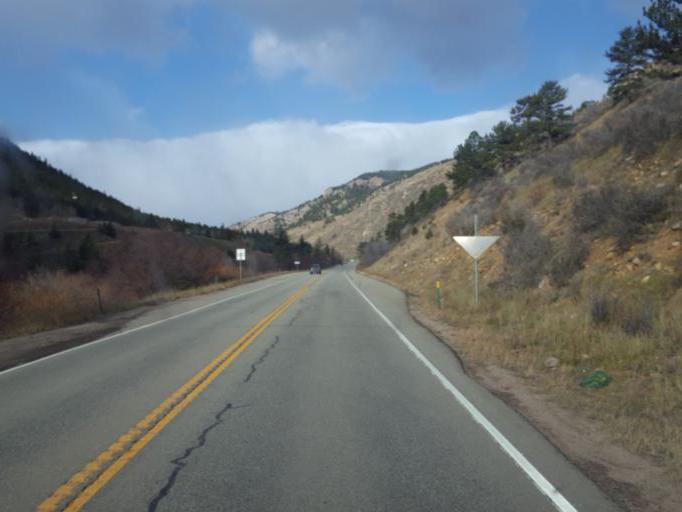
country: US
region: Colorado
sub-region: Clear Creek County
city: Georgetown
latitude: 39.4600
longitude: -105.6655
